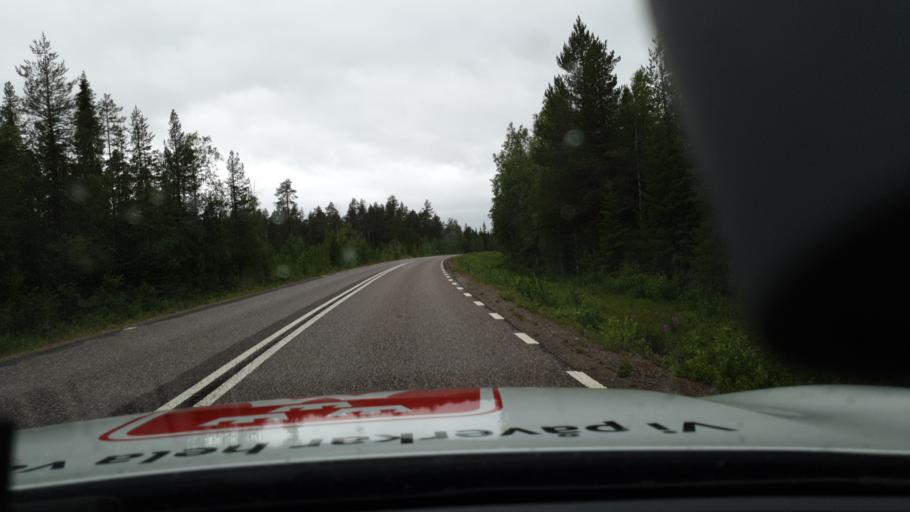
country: SE
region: Norrbotten
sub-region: Pajala Kommun
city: Pajala
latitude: 67.1656
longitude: 23.5281
